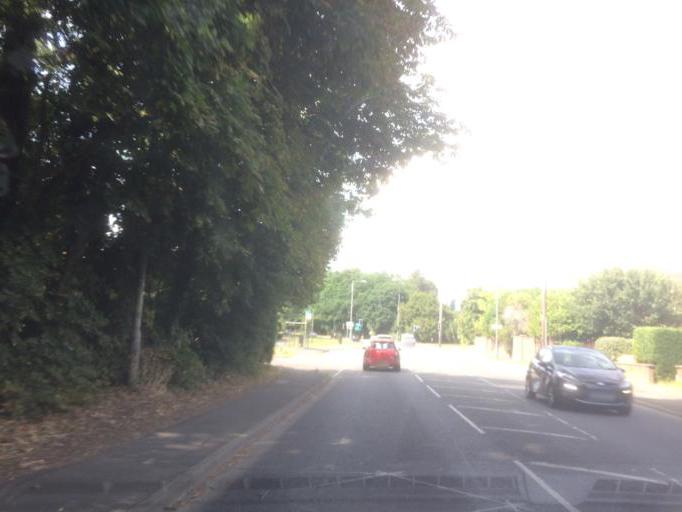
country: GB
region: England
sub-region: Buckinghamshire
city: Farnham Royal
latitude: 51.5626
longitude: -0.6153
